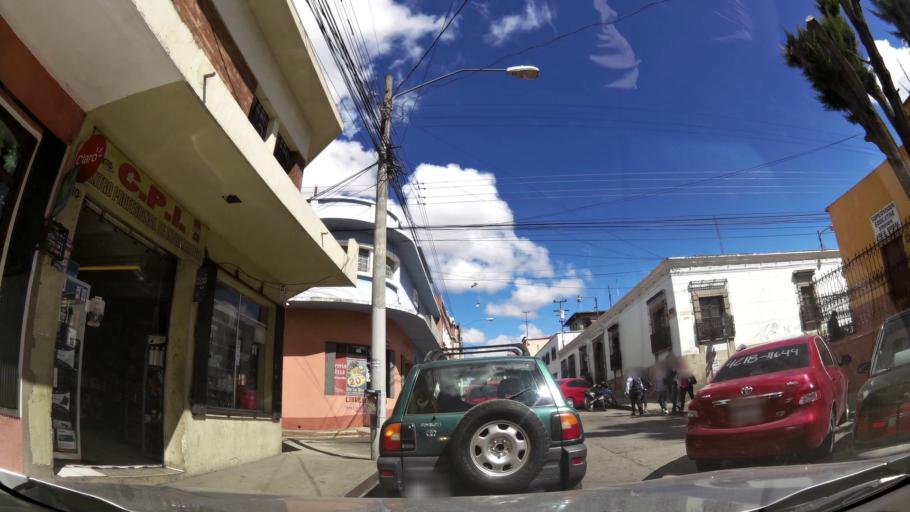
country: GT
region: Quetzaltenango
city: Quetzaltenango
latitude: 14.8367
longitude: -91.5190
